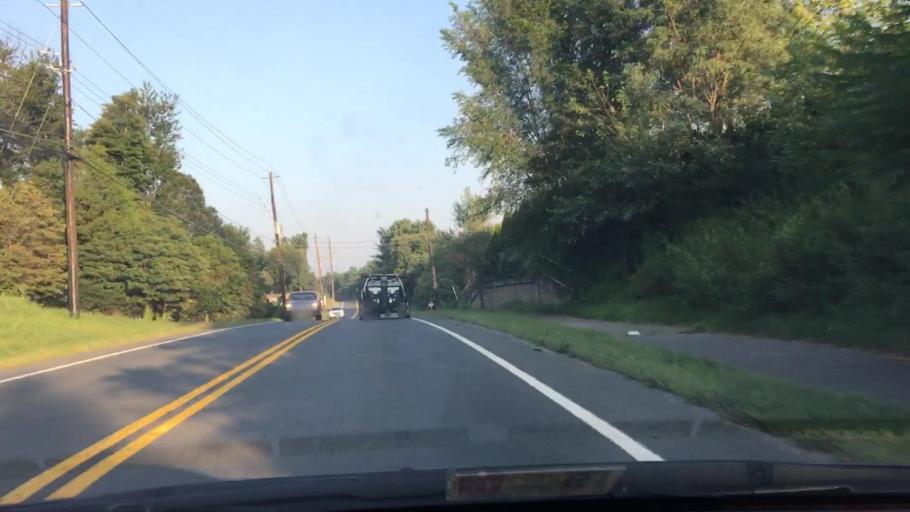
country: US
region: Maryland
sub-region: Montgomery County
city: Redland
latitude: 39.1203
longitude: -77.1110
